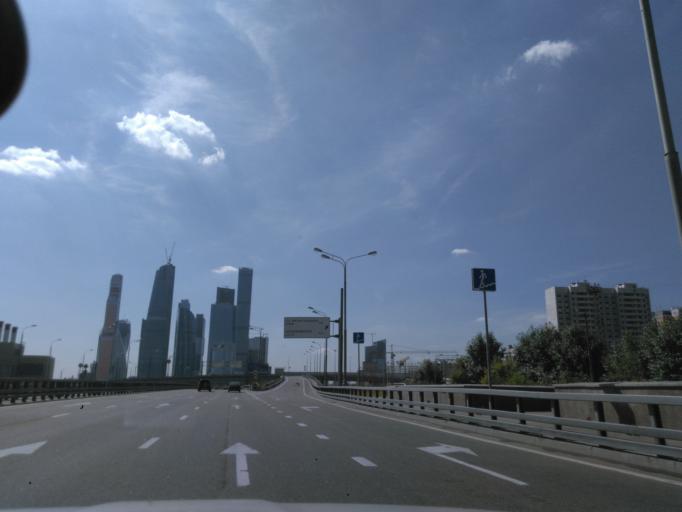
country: RU
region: Moskovskaya
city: Presnenskiy
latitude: 55.7625
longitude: 37.5221
